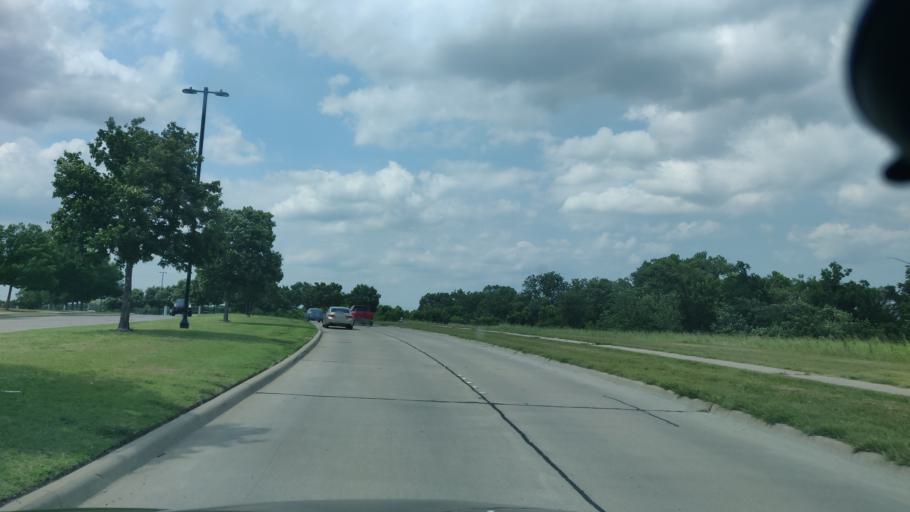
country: US
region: Texas
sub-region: Dallas County
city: Sachse
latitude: 32.9521
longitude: -96.6074
